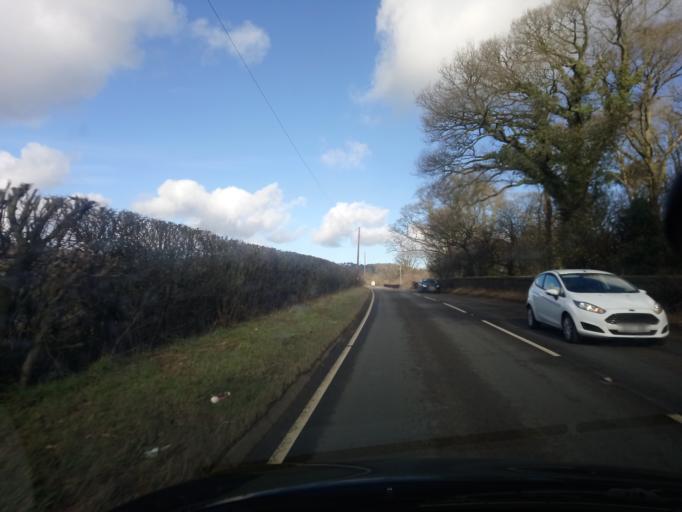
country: GB
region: England
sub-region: Shropshire
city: Clive
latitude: 52.7989
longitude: -2.6997
